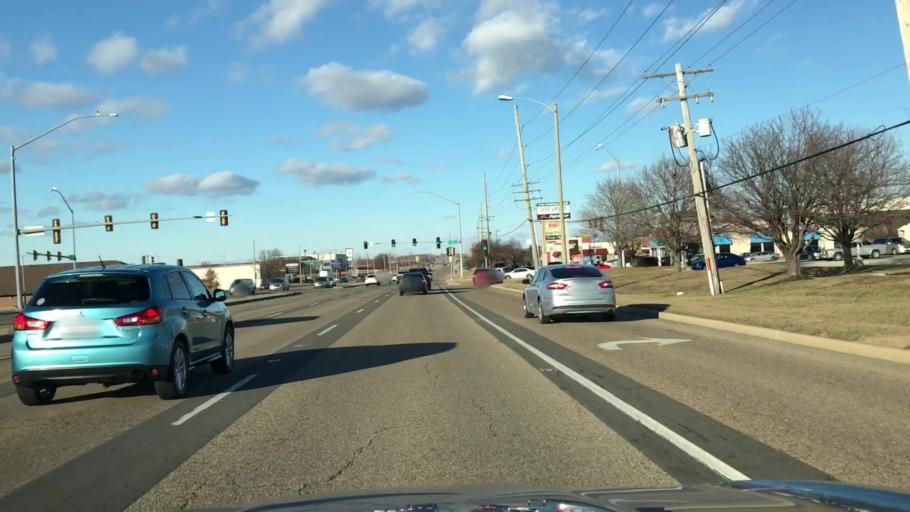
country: US
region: Illinois
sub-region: McLean County
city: Normal
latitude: 40.5131
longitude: -88.9532
